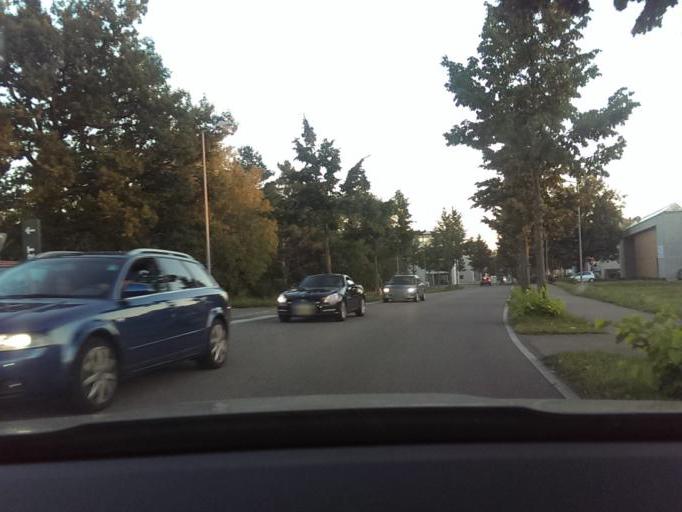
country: DE
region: Baden-Wuerttemberg
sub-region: Karlsruhe Region
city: Karlsruhe
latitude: 49.0342
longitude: 8.3938
